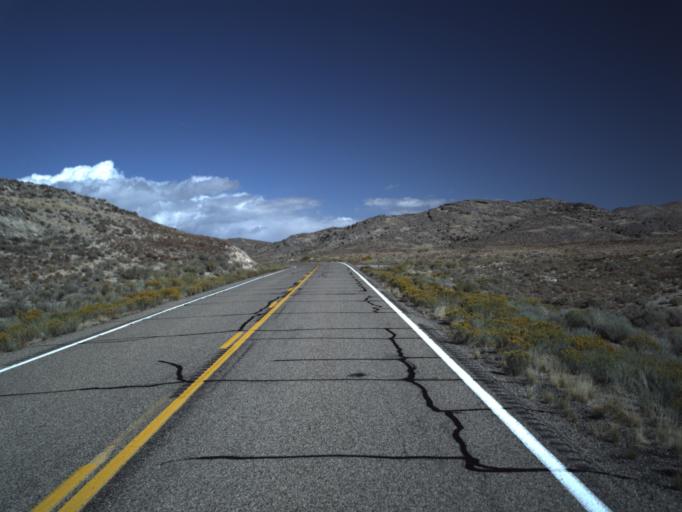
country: US
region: Nevada
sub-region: White Pine County
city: McGill
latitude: 38.8964
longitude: -114.0128
